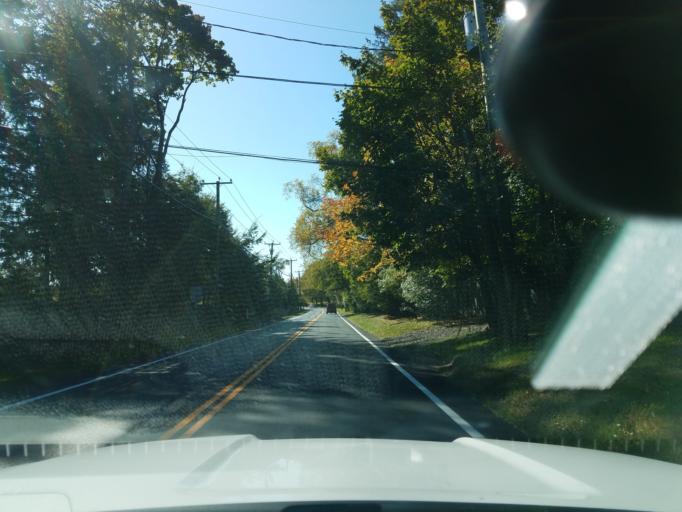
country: US
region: Connecticut
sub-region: Fairfield County
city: Cos Cob
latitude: 41.0765
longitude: -73.6238
